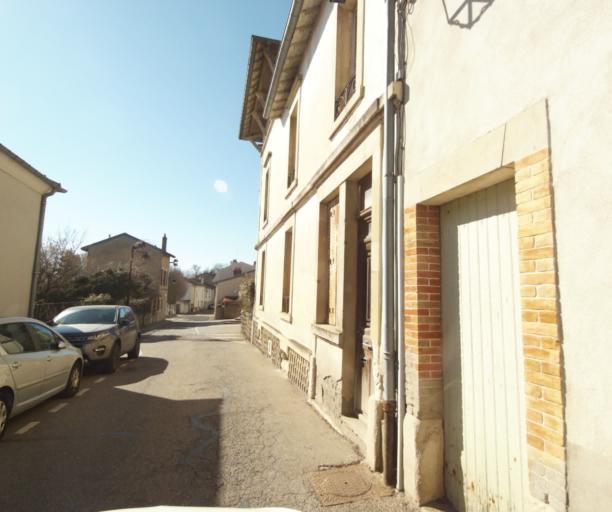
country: FR
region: Lorraine
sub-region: Departement de Meurthe-et-Moselle
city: Saint-Max
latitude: 48.7132
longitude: 6.2156
